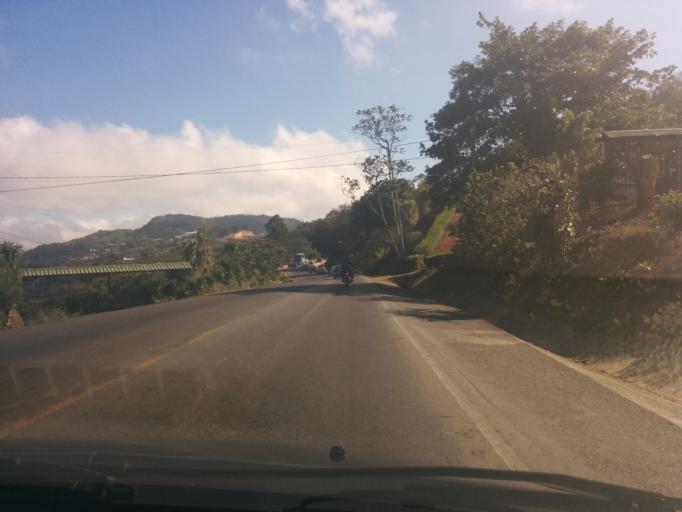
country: CR
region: Alajuela
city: San Rafael
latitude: 10.0523
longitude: -84.5046
